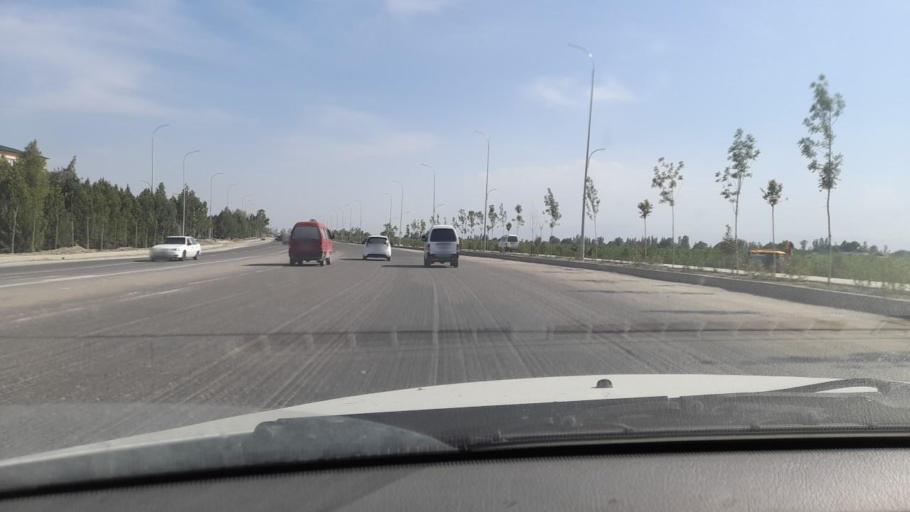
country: UZ
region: Samarqand
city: Daxbet
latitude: 39.7549
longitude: 66.9192
